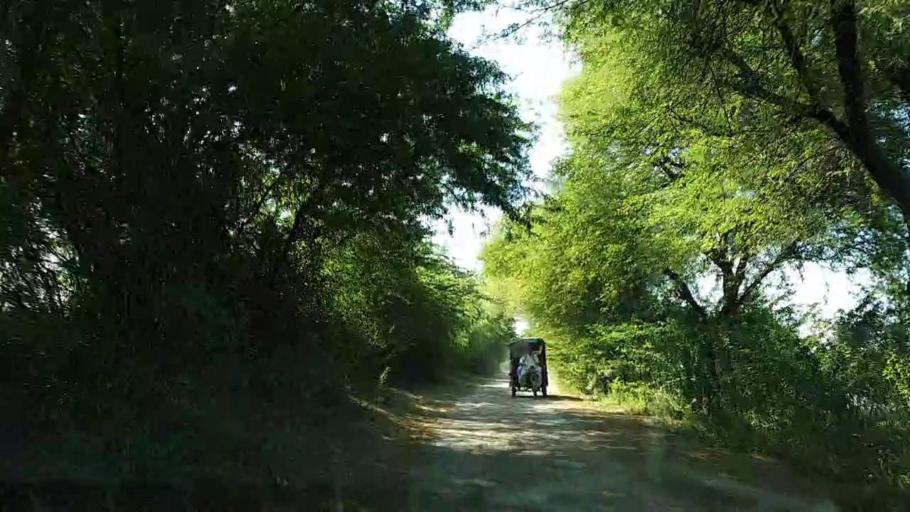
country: PK
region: Sindh
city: Chuhar Jamali
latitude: 24.5743
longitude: 68.0447
